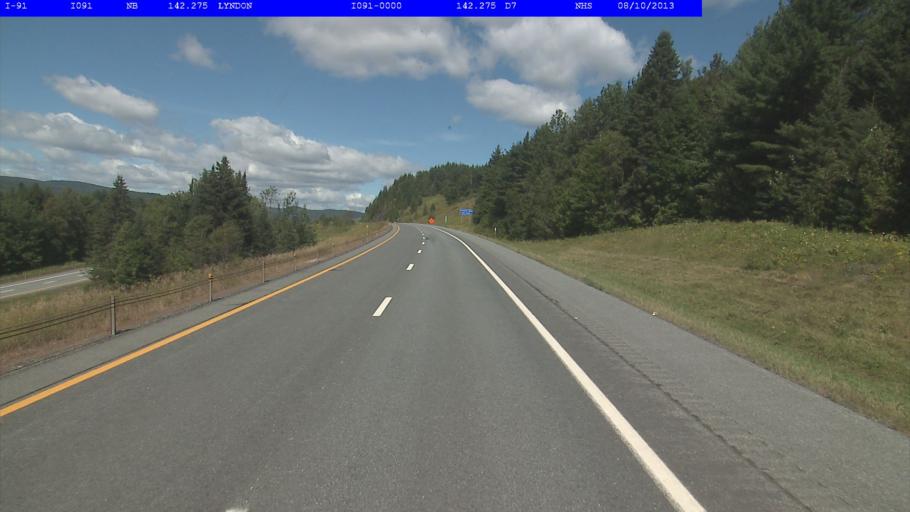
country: US
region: Vermont
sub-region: Caledonia County
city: Lyndonville
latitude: 44.5801
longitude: -72.0531
